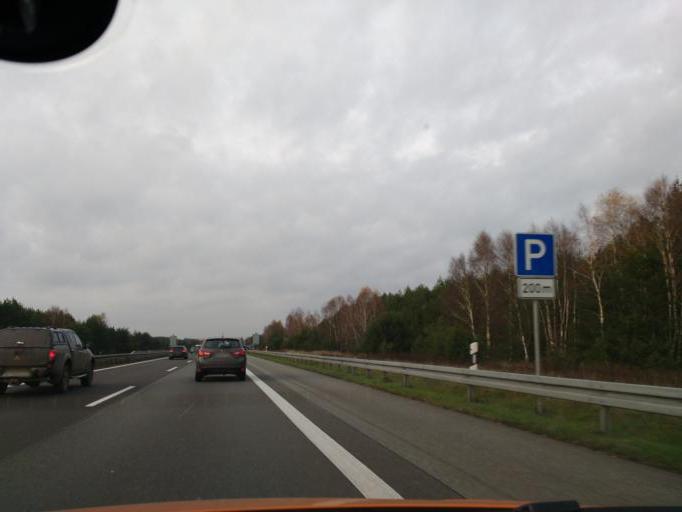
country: DE
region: Brandenburg
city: Walsleben
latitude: 53.0051
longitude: 12.5939
